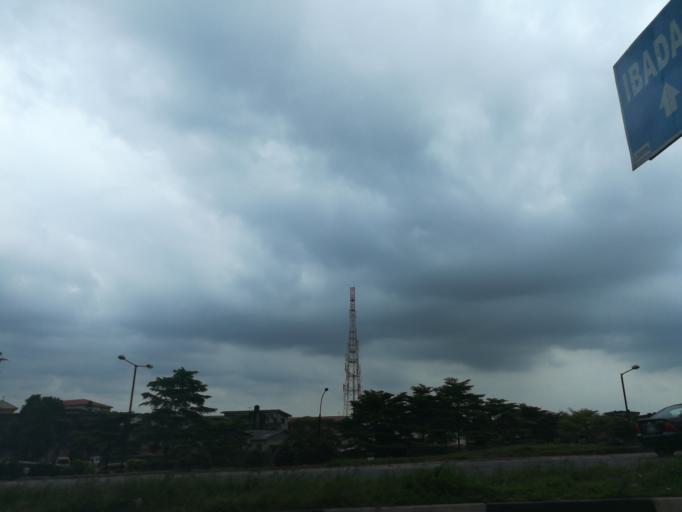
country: NG
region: Lagos
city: Somolu
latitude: 6.5502
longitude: 3.3948
